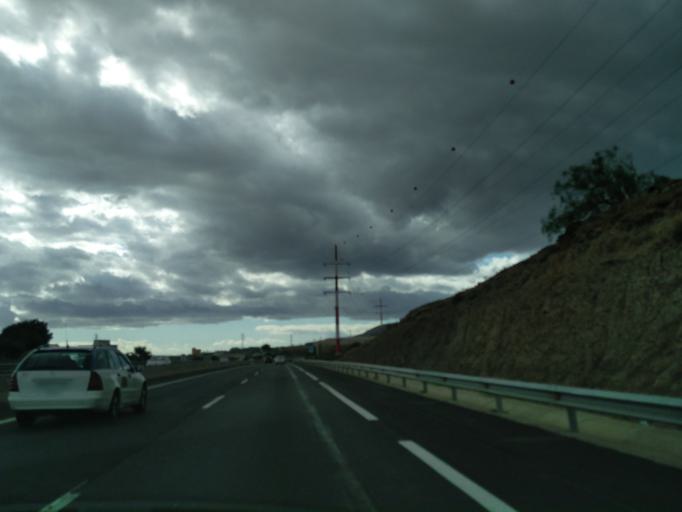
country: ES
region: Canary Islands
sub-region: Provincia de Santa Cruz de Tenerife
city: Las Rosas
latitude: 28.0503
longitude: -16.6234
